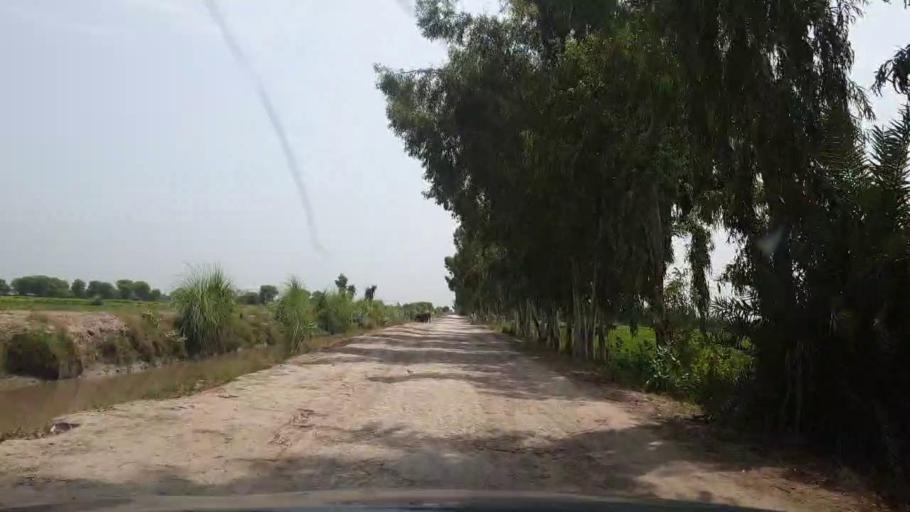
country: PK
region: Sindh
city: Ratodero
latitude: 27.8802
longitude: 68.3420
